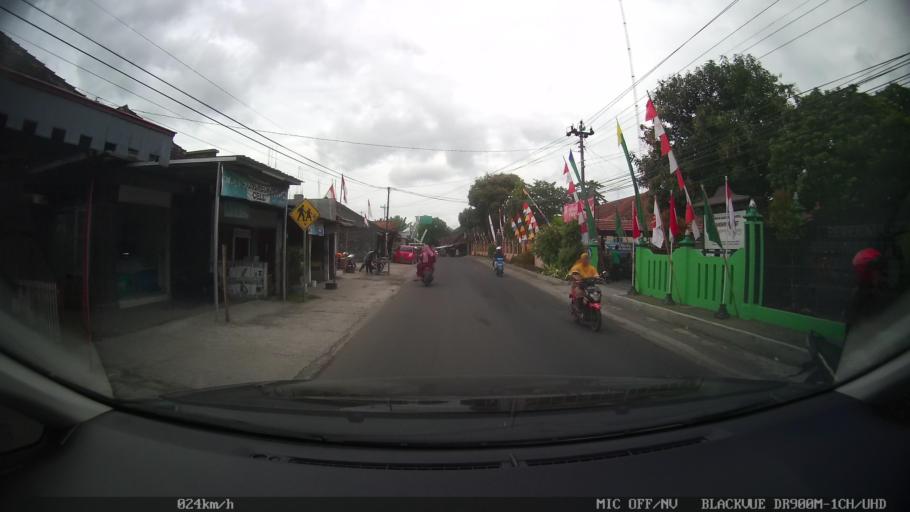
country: ID
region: Daerah Istimewa Yogyakarta
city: Sewon
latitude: -7.8662
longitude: 110.4078
